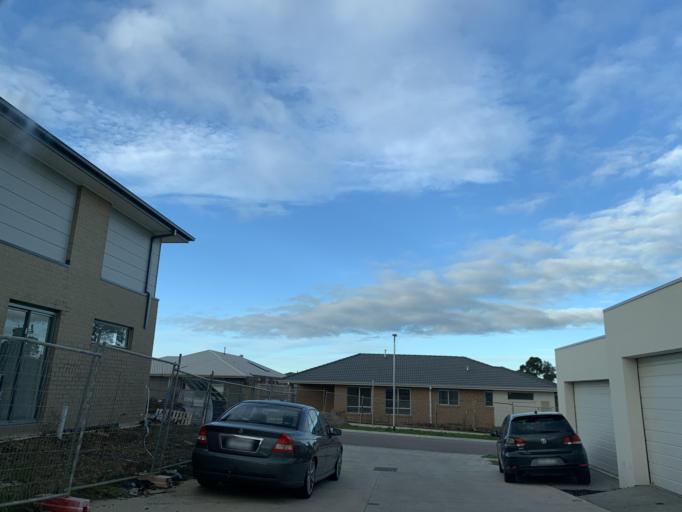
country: AU
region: Victoria
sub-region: Casey
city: Junction Village
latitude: -38.1293
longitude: 145.3065
